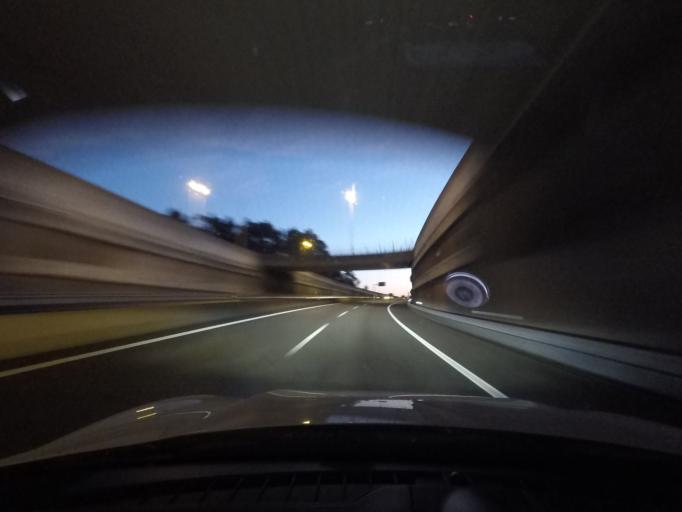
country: PT
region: Aveiro
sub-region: Santa Maria da Feira
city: Argoncilhe
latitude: 41.0103
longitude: -8.5550
